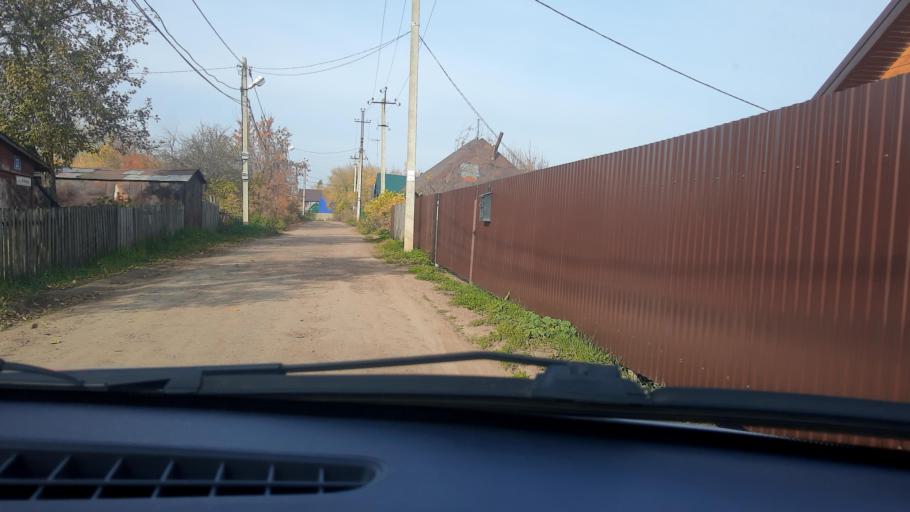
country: RU
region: Bashkortostan
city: Ufa
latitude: 54.7920
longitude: 56.0918
